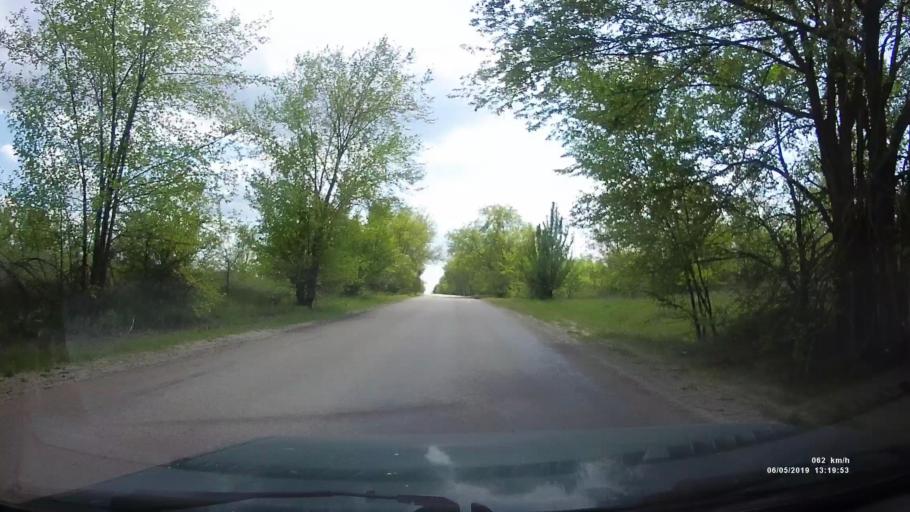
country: RU
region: Rostov
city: Ust'-Donetskiy
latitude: 47.7215
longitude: 40.9124
